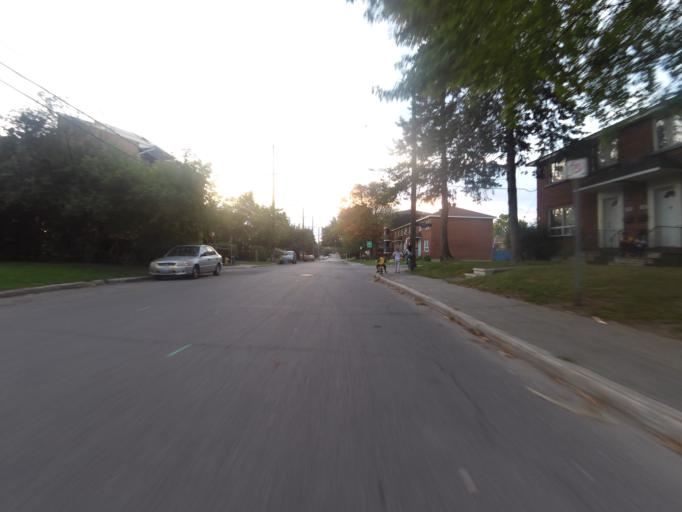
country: CA
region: Ontario
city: Ottawa
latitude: 45.4231
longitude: -75.6555
